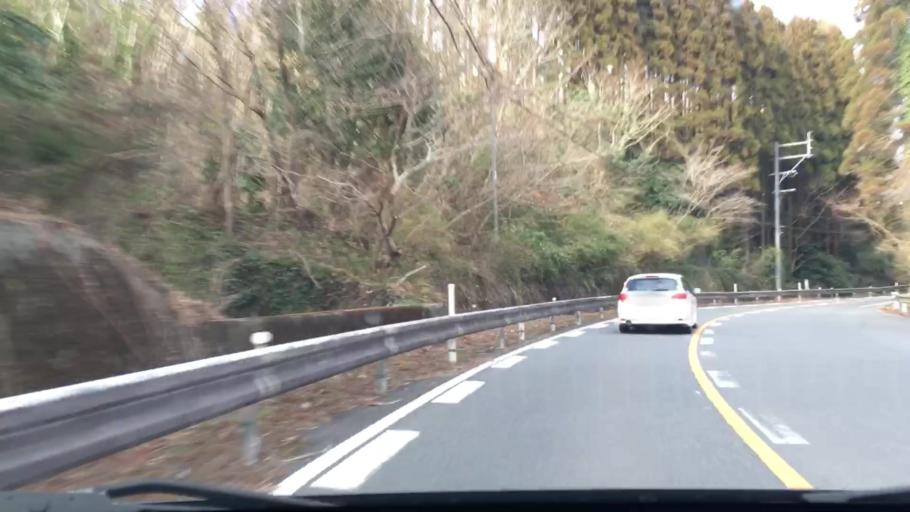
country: JP
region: Miyazaki
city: Nichinan
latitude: 31.7299
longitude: 131.3304
